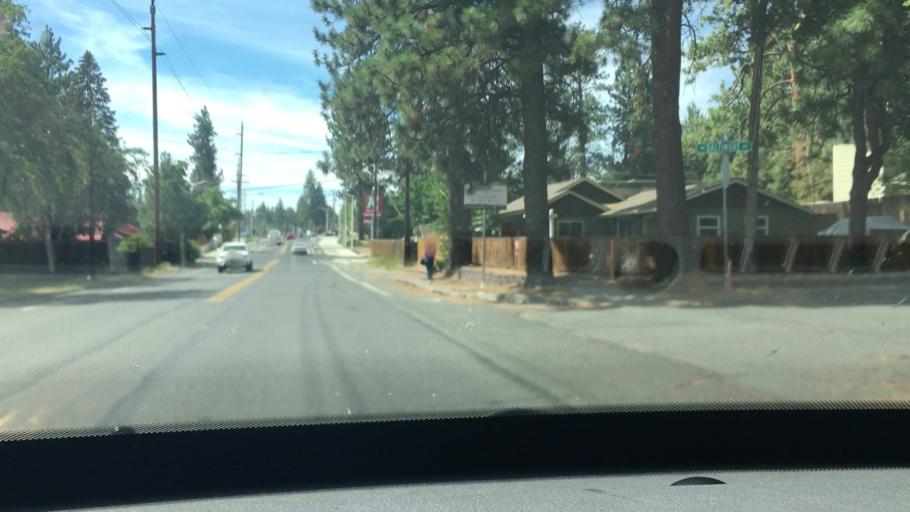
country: US
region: Oregon
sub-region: Deschutes County
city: Bend
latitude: 44.0528
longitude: -121.3319
